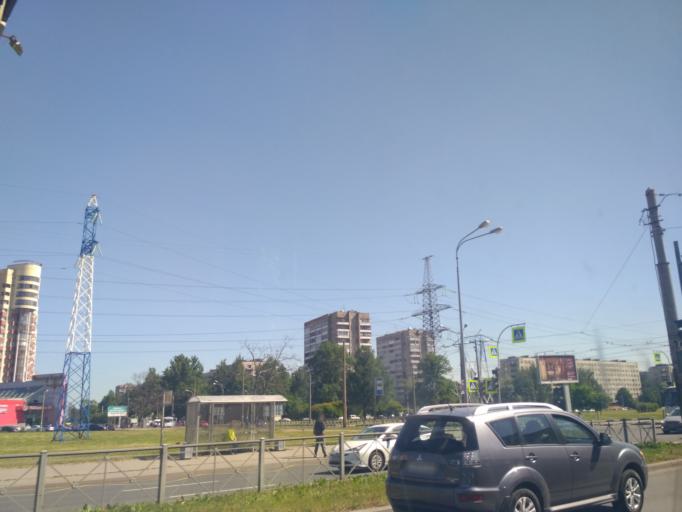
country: RU
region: Leningrad
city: Kalininskiy
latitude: 59.9777
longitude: 30.3923
